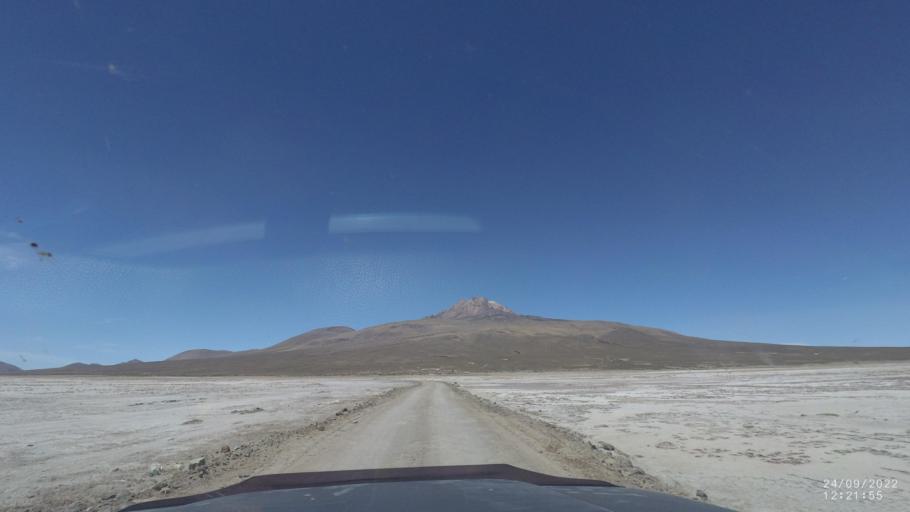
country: BO
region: Potosi
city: Colchani
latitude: -19.7522
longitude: -67.6674
